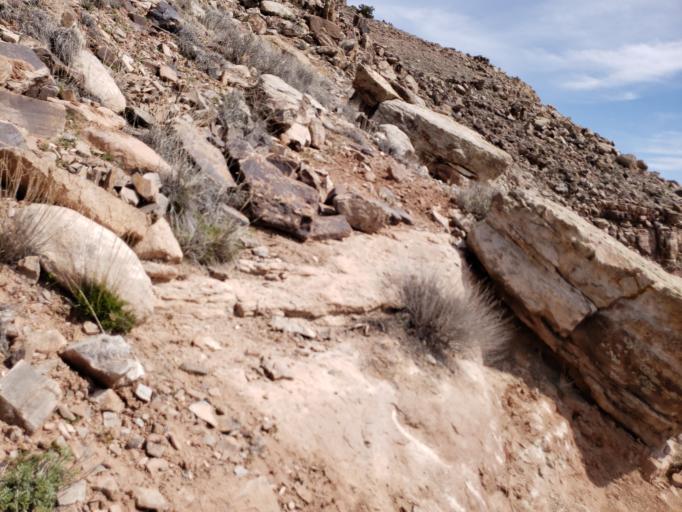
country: US
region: Colorado
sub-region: Mesa County
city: Loma
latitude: 39.1833
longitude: -108.8537
